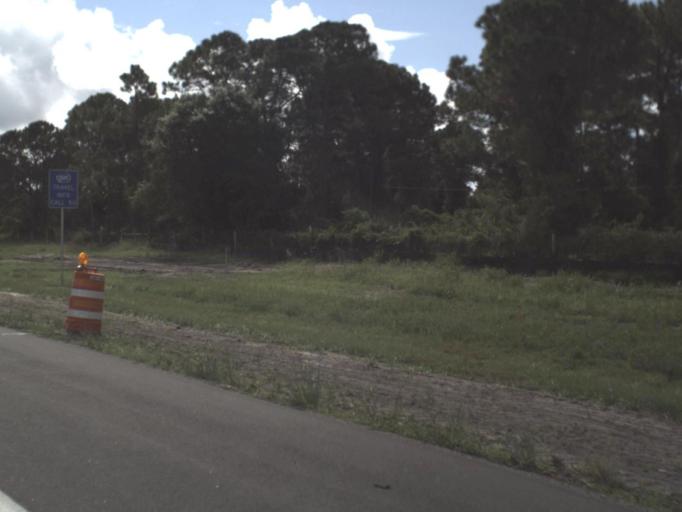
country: US
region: Florida
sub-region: Sarasota County
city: Warm Mineral Springs
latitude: 27.0994
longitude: -82.2250
